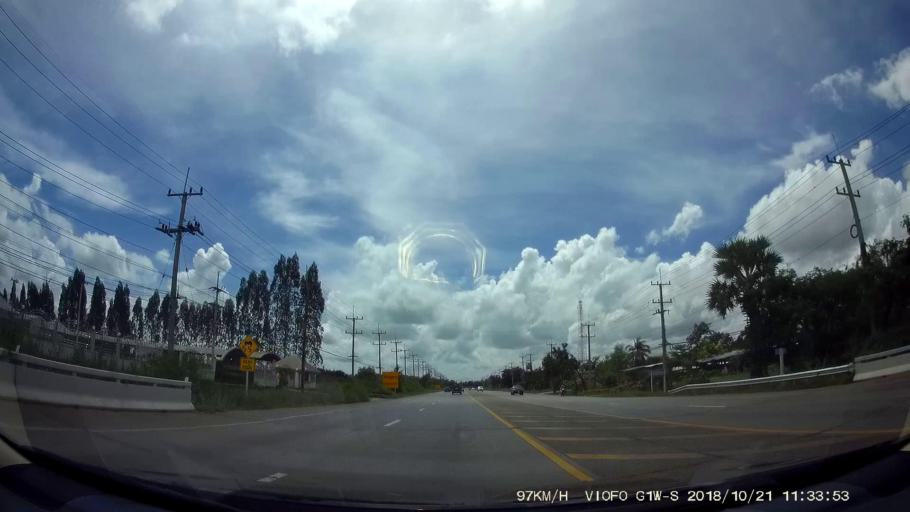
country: TH
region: Chaiyaphum
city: Chaiyaphum
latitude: 15.7393
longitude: 102.0243
